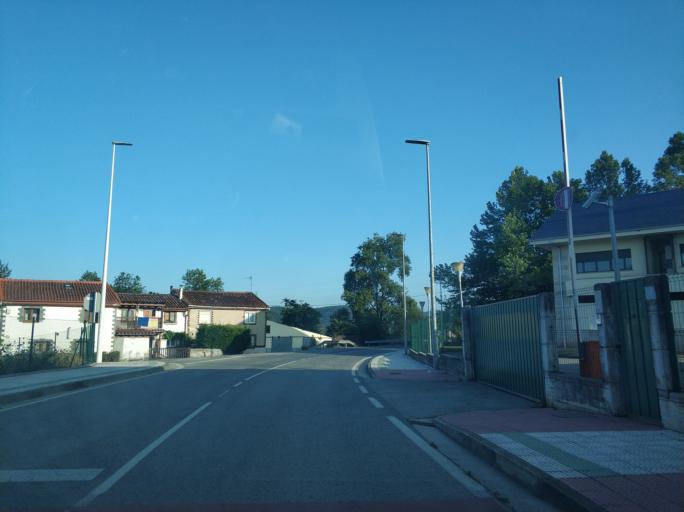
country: ES
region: Cantabria
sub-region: Provincia de Cantabria
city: Puente Viesgo
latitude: 43.3576
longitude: -3.9551
